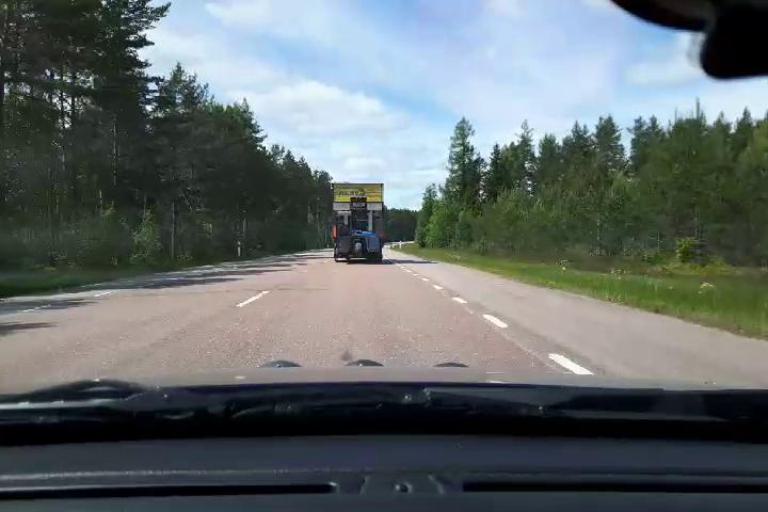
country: SE
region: Uppsala
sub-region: Osthammars Kommun
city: Bjorklinge
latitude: 60.1116
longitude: 17.5292
